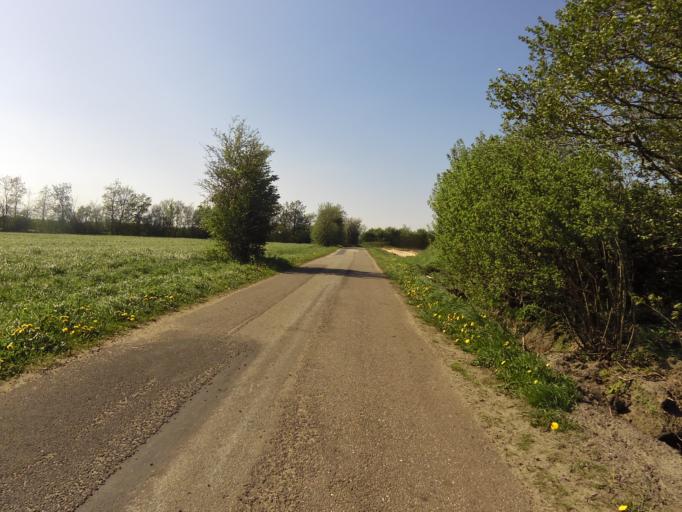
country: DK
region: South Denmark
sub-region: Tonder Kommune
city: Sherrebek
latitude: 55.2126
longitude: 8.8416
